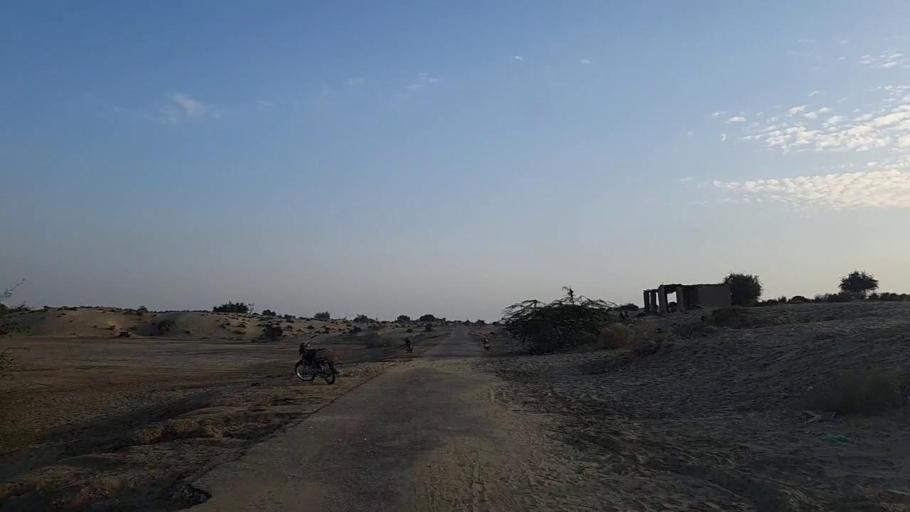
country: PK
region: Sindh
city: Jam Sahib
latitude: 26.3978
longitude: 68.5005
